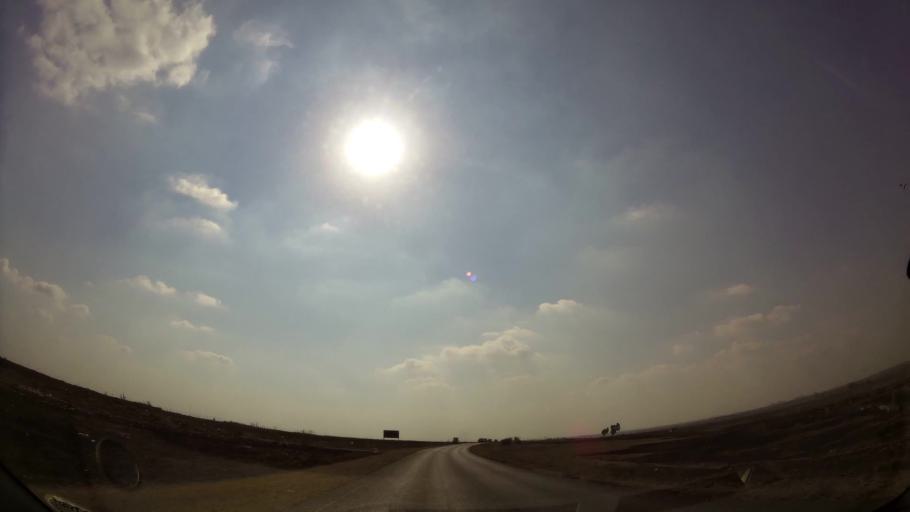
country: ZA
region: Gauteng
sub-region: Ekurhuleni Metropolitan Municipality
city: Springs
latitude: -26.1442
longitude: 28.4459
